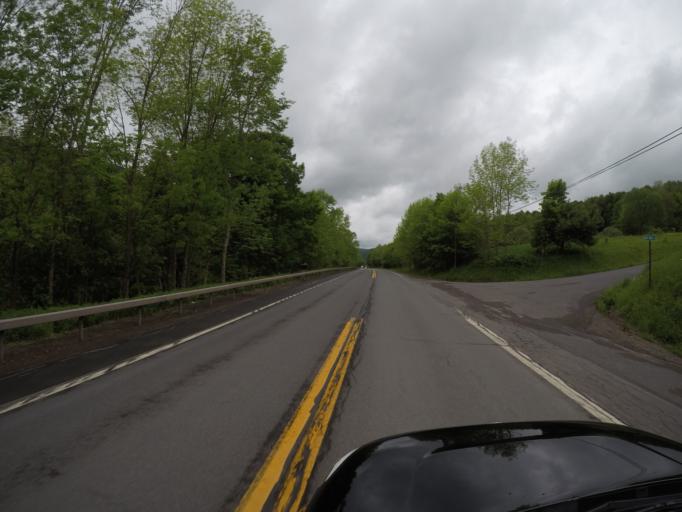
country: US
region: New York
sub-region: Delaware County
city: Delhi
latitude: 42.2531
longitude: -74.8500
